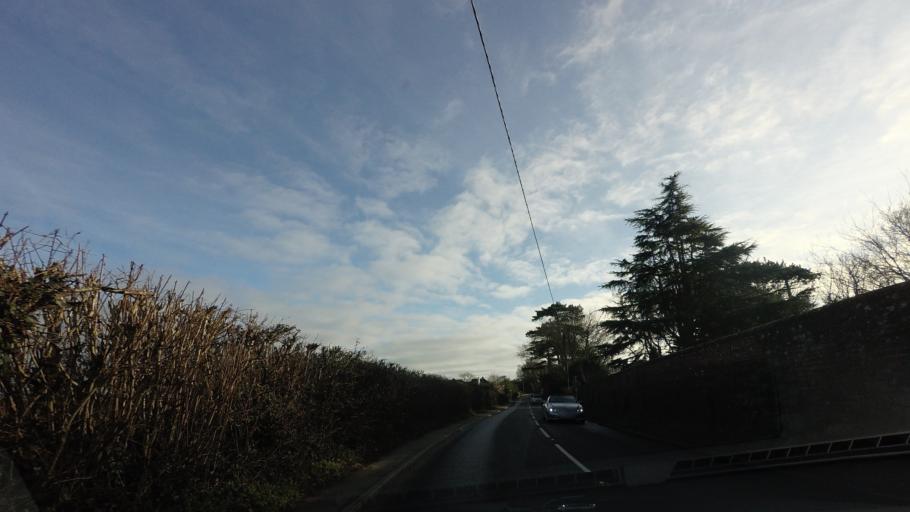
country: GB
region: England
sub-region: East Sussex
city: Bexhill-on-Sea
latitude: 50.8695
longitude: 0.4448
